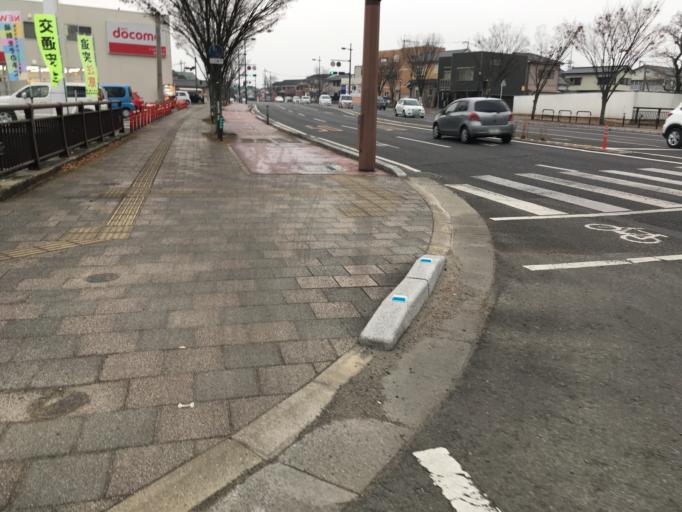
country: JP
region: Saga Prefecture
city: Saga-shi
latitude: 33.2550
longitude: 130.2929
